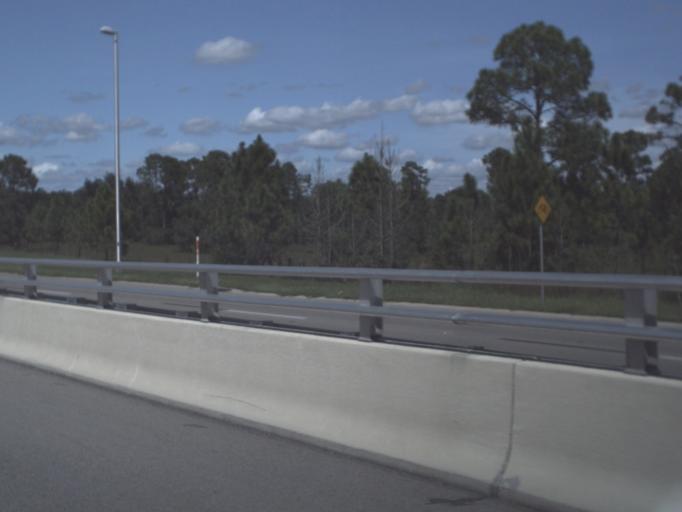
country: US
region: Florida
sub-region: Lee County
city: San Carlos Park
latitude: 26.4987
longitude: -81.8446
